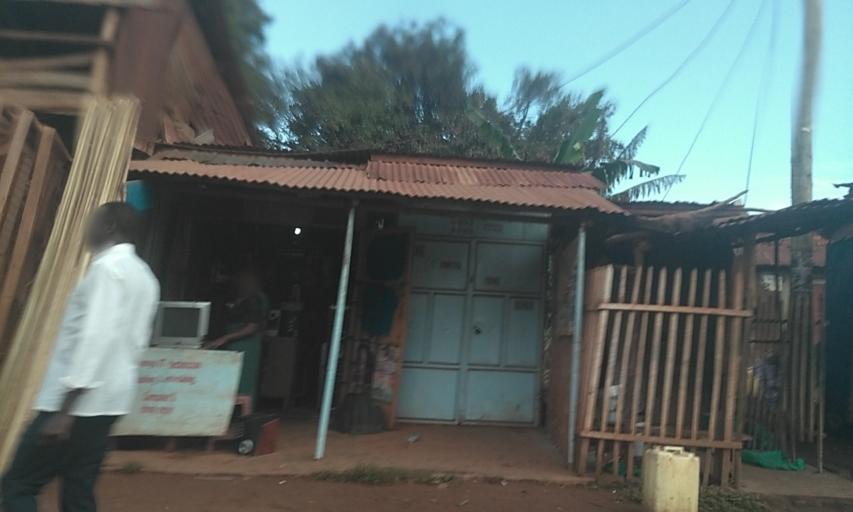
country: UG
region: Central Region
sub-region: Wakiso District
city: Kajansi
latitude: 0.2580
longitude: 32.5081
